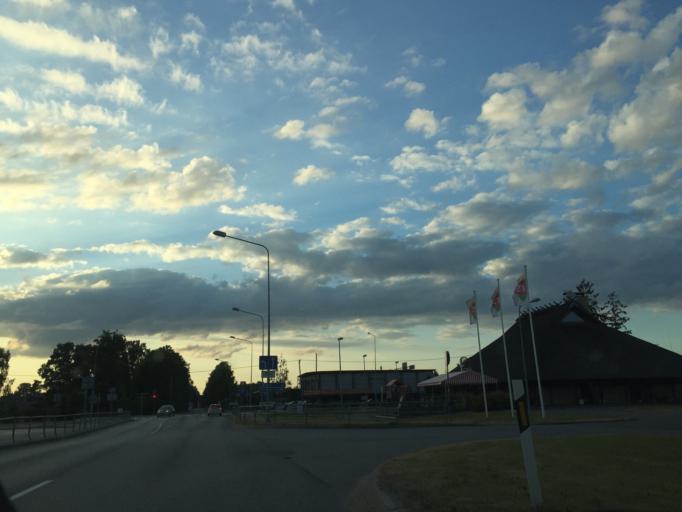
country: LV
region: Sigulda
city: Sigulda
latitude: 57.1446
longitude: 24.8588
